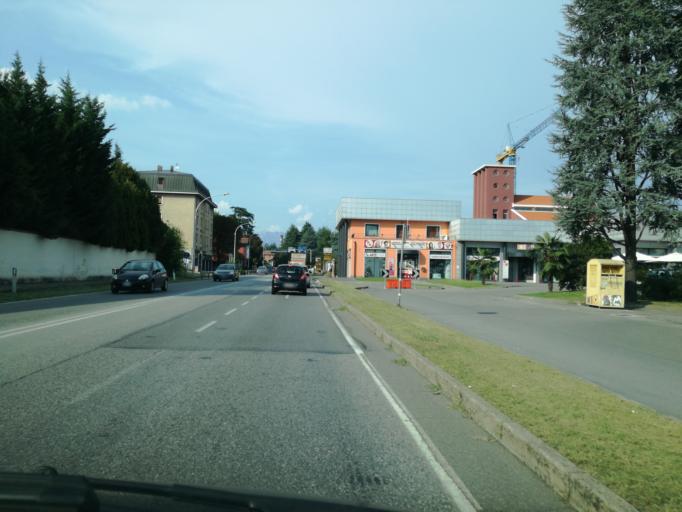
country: IT
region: Lombardy
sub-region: Provincia di Lecco
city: Cernusco Lombardone
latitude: 45.6912
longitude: 9.4014
